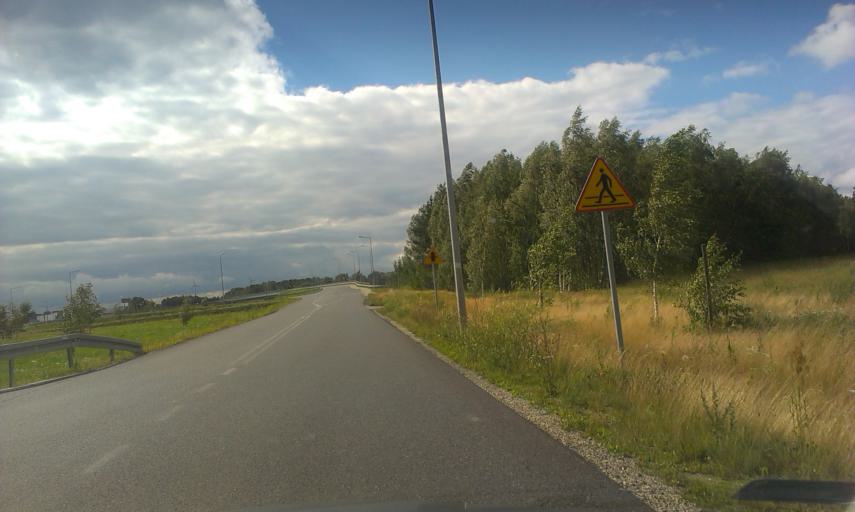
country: PL
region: Masovian Voivodeship
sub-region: Powiat zyrardowski
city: Radziejowice
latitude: 51.9706
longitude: 20.5764
